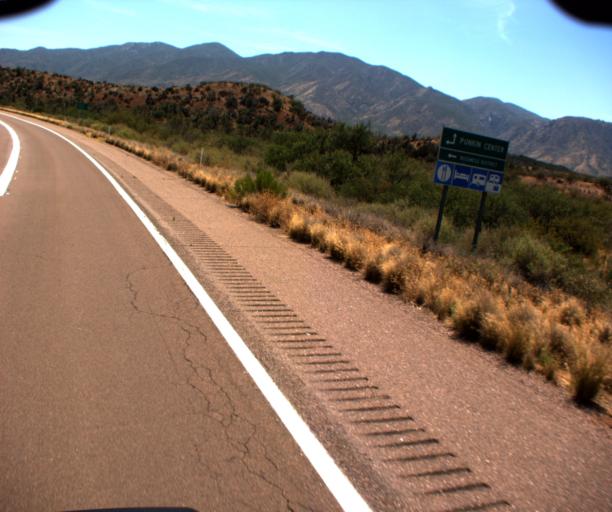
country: US
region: Arizona
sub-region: Gila County
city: Tonto Basin
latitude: 33.8782
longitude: -111.3153
